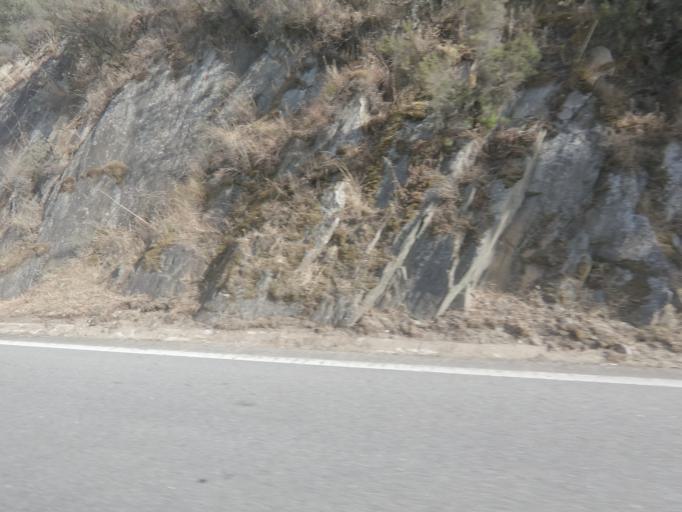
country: PT
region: Vila Real
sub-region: Sabrosa
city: Vilela
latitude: 41.1574
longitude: -7.6287
